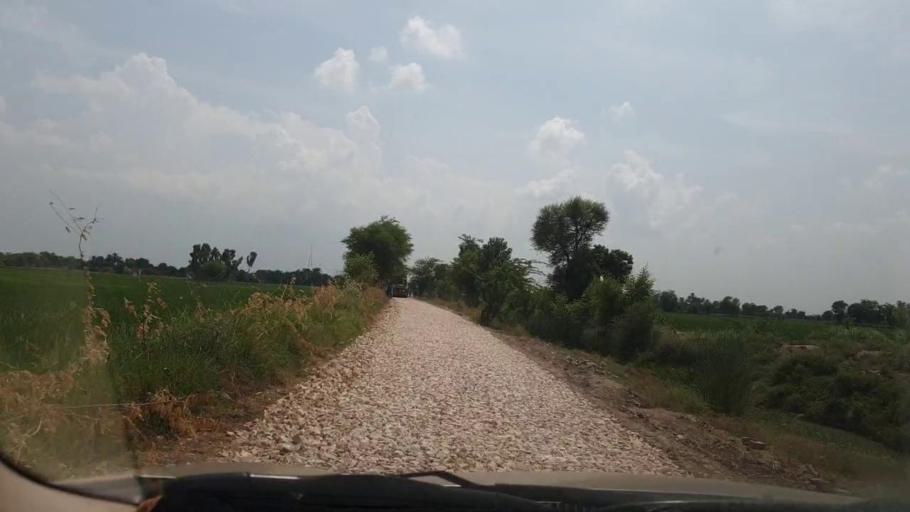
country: PK
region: Sindh
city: Larkana
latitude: 27.5668
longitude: 68.1100
